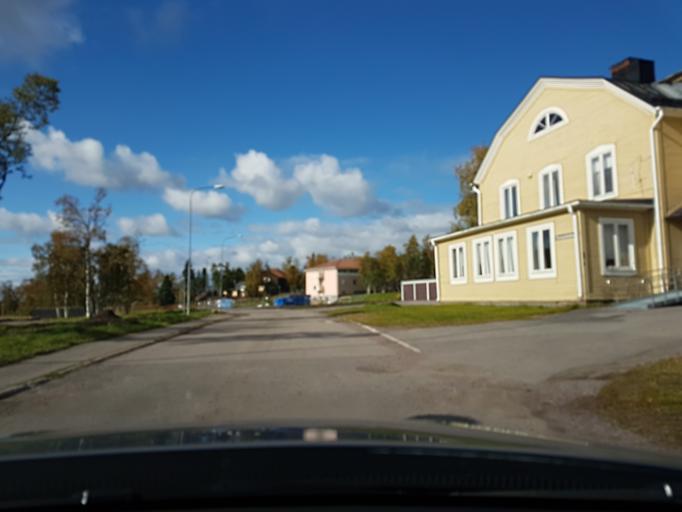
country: SE
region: Norrbotten
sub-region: Kiruna Kommun
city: Kiruna
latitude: 67.8464
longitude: 20.2267
